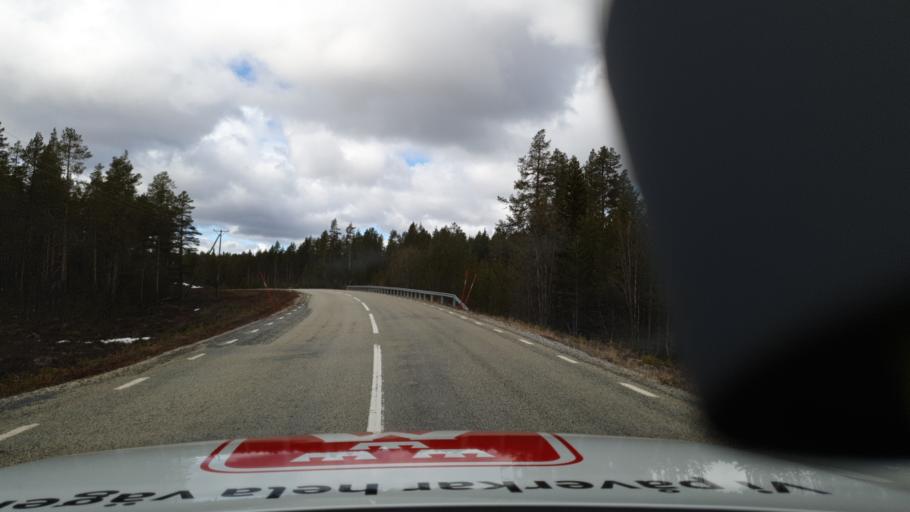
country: SE
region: Jaemtland
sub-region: Are Kommun
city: Jarpen
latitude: 62.8137
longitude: 13.6394
